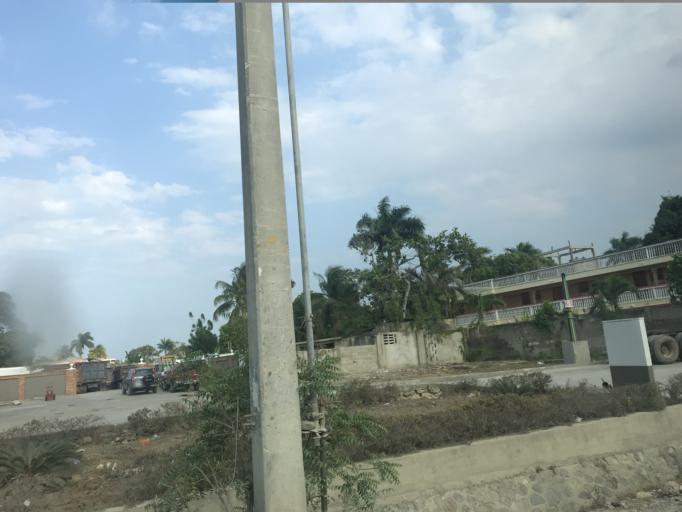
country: HT
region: Nord
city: Quartier Morin
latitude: 19.7217
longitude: -72.1816
